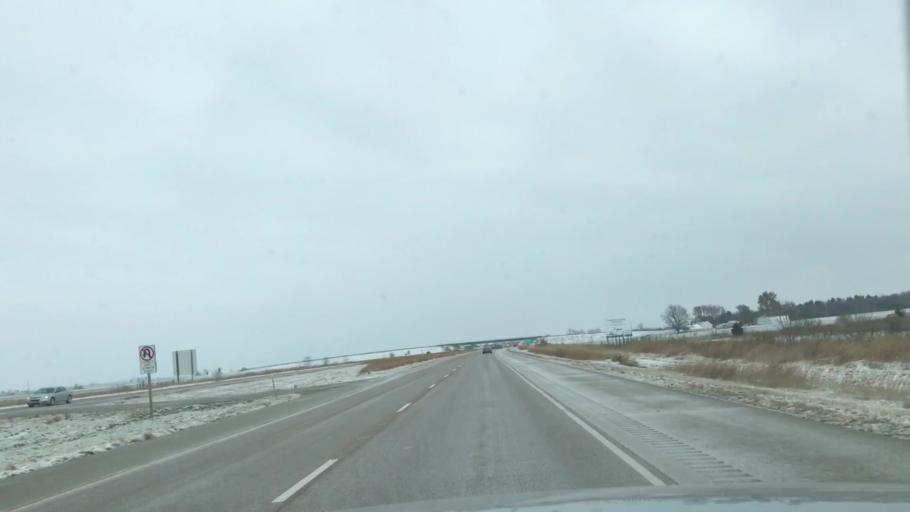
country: US
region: Illinois
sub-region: Montgomery County
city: Litchfield
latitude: 39.1842
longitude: -89.6748
